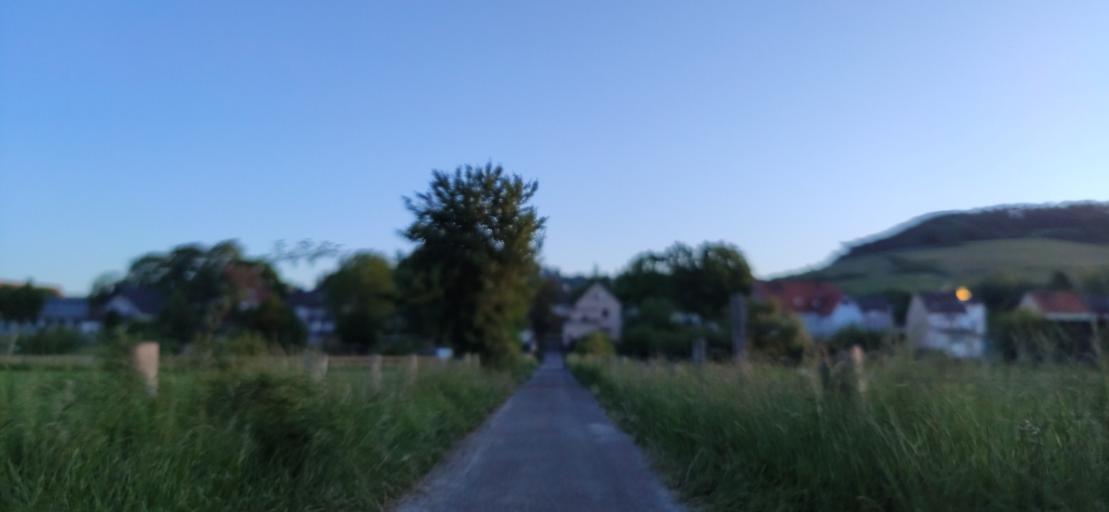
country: DE
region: North Rhine-Westphalia
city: Beverungen
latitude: 51.7075
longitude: 9.3106
